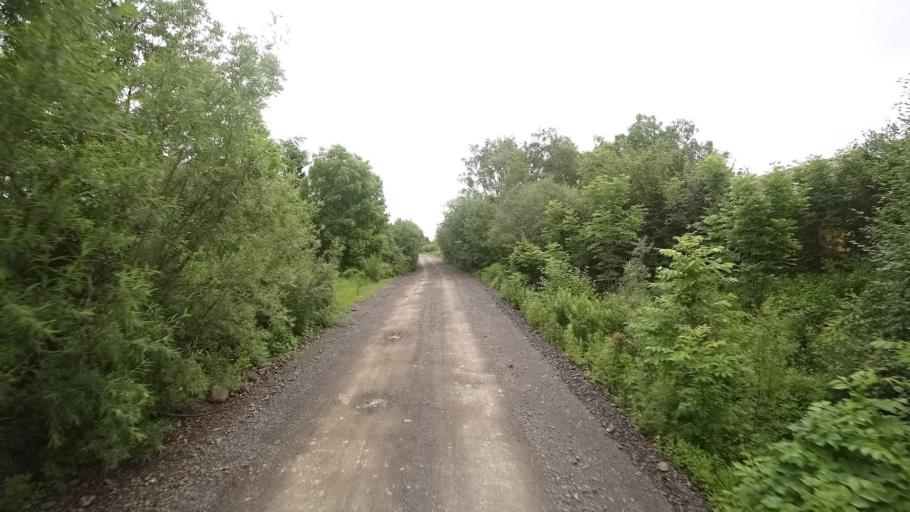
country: RU
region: Khabarovsk Krai
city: Amursk
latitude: 49.8967
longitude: 136.1291
